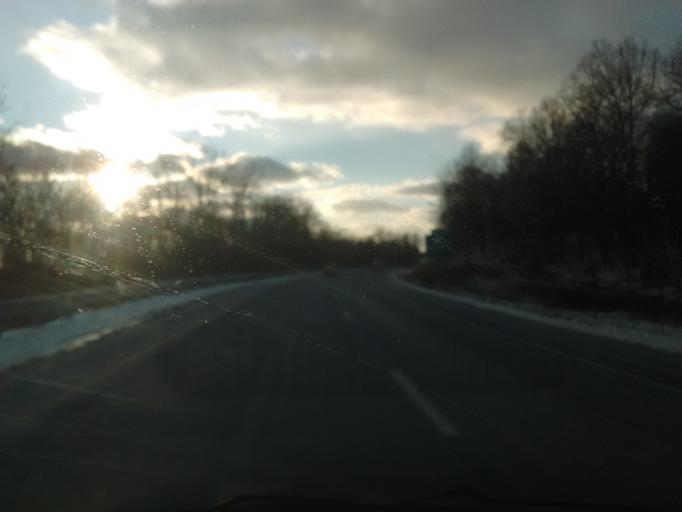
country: US
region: Pennsylvania
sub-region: Pike County
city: Milford
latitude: 41.3439
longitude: -74.7976
